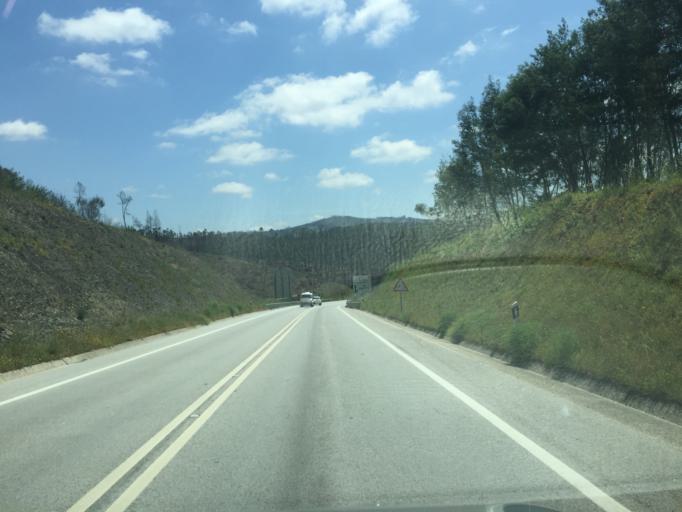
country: PT
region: Castelo Branco
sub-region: Serta
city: Serta
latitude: 39.8114
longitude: -8.0841
